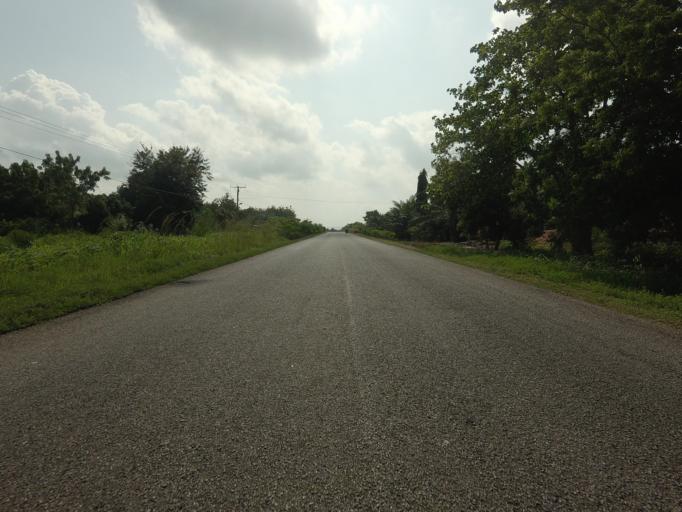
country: GH
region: Volta
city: Ho
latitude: 6.5797
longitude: 0.5807
